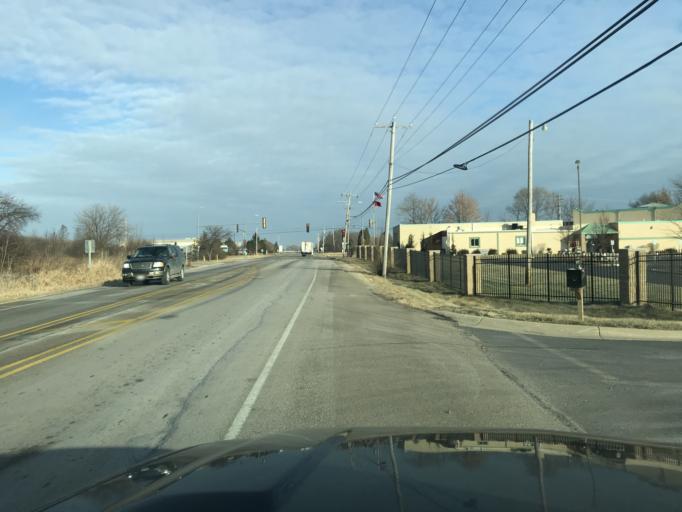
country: US
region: Wisconsin
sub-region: Kenosha County
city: Pleasant Prairie
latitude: 42.5810
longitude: -87.9146
